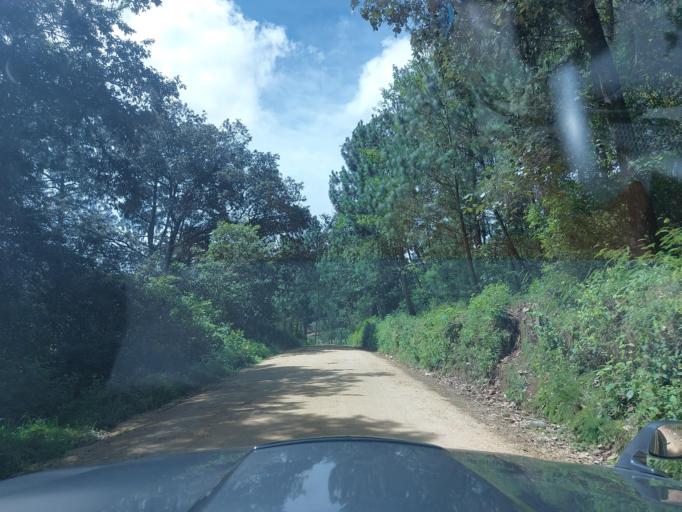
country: GT
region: Chimaltenango
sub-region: Municipio de San Juan Comalapa
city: Comalapa
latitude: 14.7535
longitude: -90.8712
